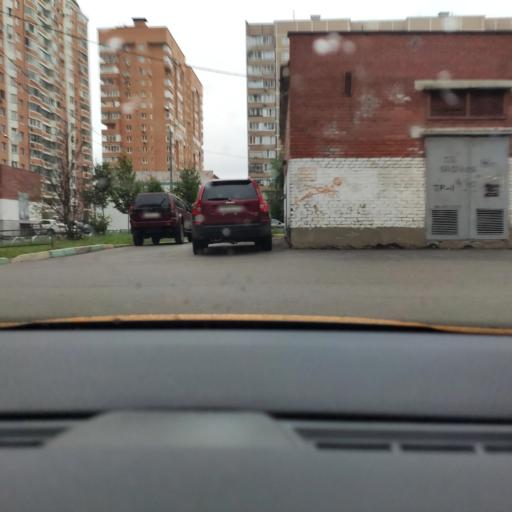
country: RU
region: Moskovskaya
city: Odintsovo
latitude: 55.6884
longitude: 37.2957
